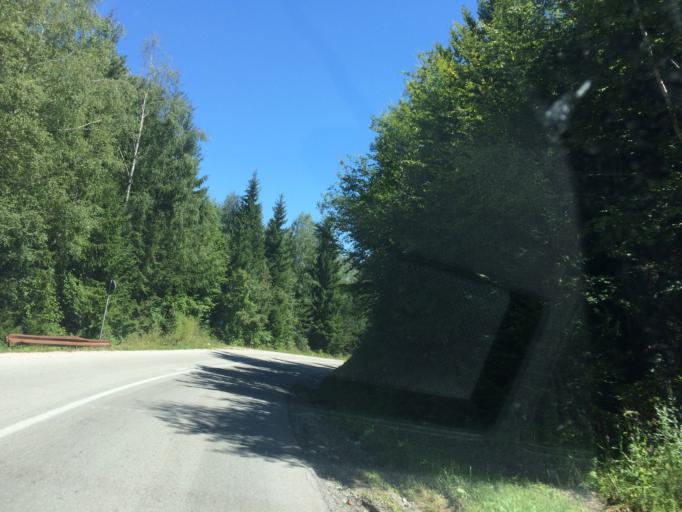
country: RS
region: Central Serbia
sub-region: Zlatiborski Okrug
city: Prijepolje
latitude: 43.3308
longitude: 19.5365
